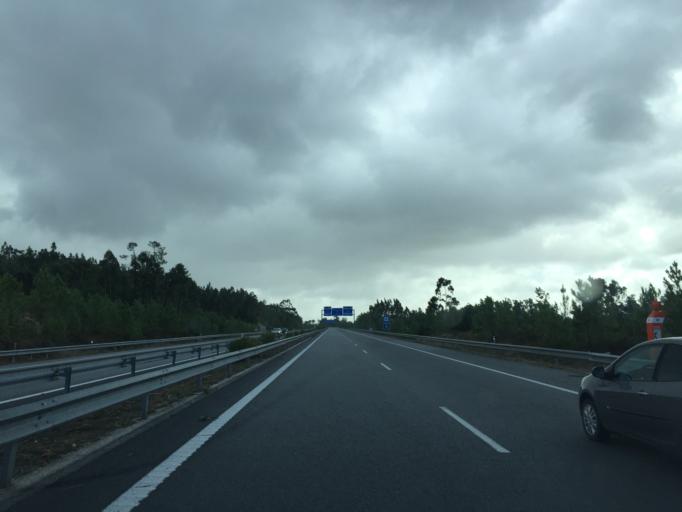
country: PT
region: Aveiro
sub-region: Mealhada
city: Pampilhosa do Botao
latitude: 40.2802
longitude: -8.5101
